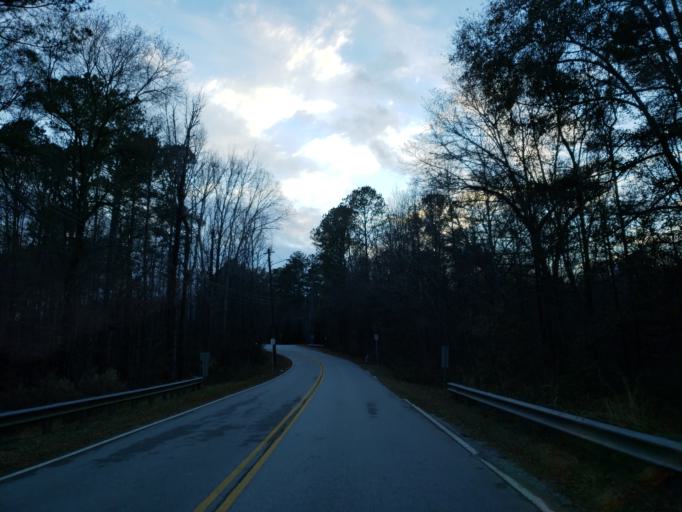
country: US
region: Georgia
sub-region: Fulton County
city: Union City
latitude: 33.6745
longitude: -84.5627
